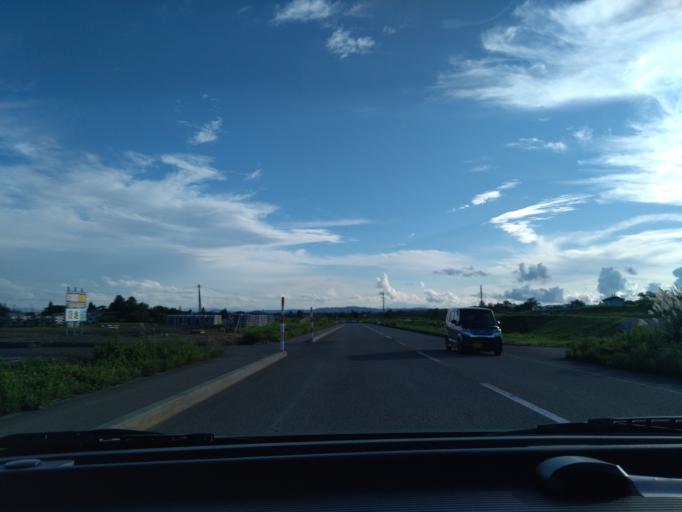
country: JP
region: Akita
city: Omagari
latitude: 39.4101
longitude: 140.4796
